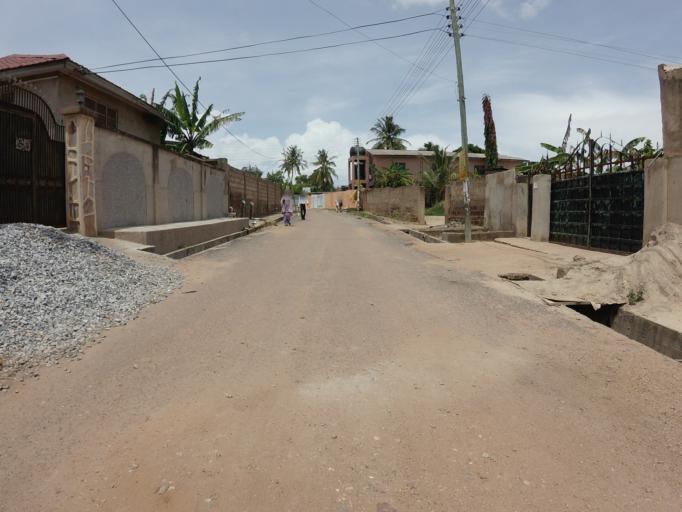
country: GH
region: Greater Accra
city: Dome
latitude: 5.6119
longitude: -0.2432
